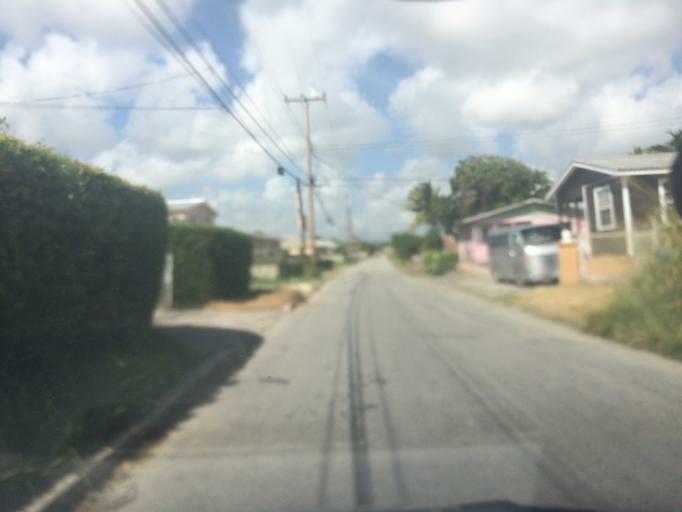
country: BB
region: Christ Church
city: Oistins
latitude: 13.0534
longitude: -59.5159
